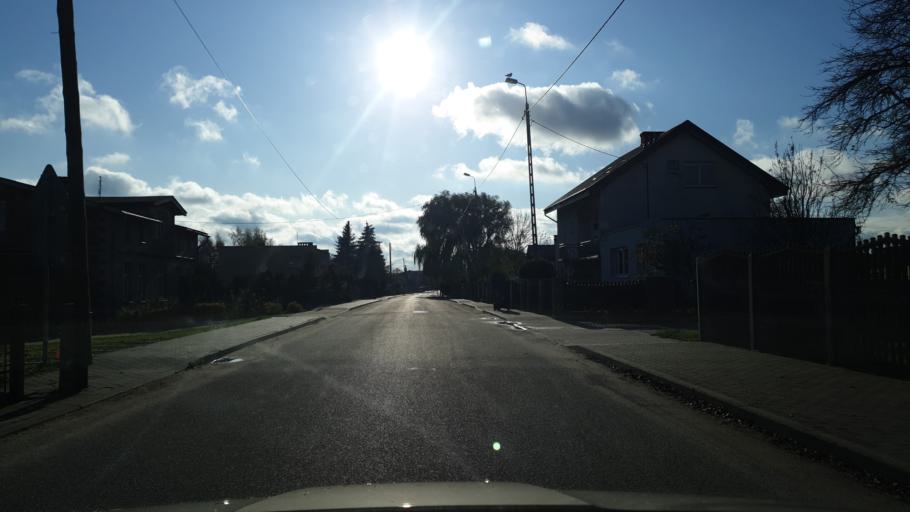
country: PL
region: Pomeranian Voivodeship
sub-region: Powiat pucki
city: Gniezdzewo
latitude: 54.7590
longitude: 18.3997
